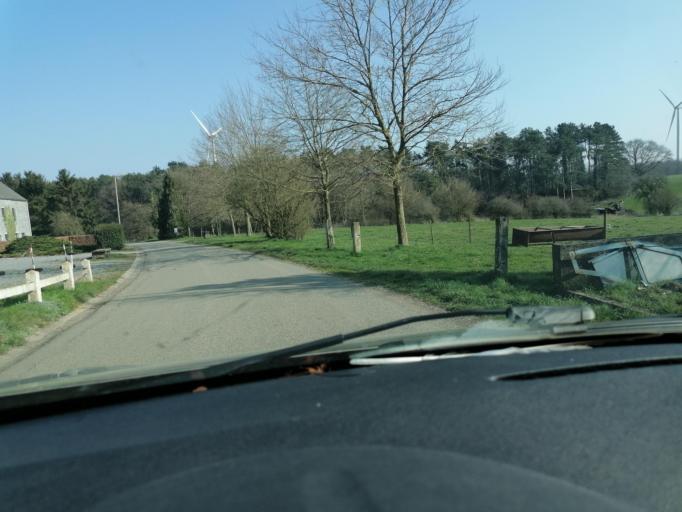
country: BE
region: Wallonia
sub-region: Province du Hainaut
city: Chimay
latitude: 50.0521
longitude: 4.3637
